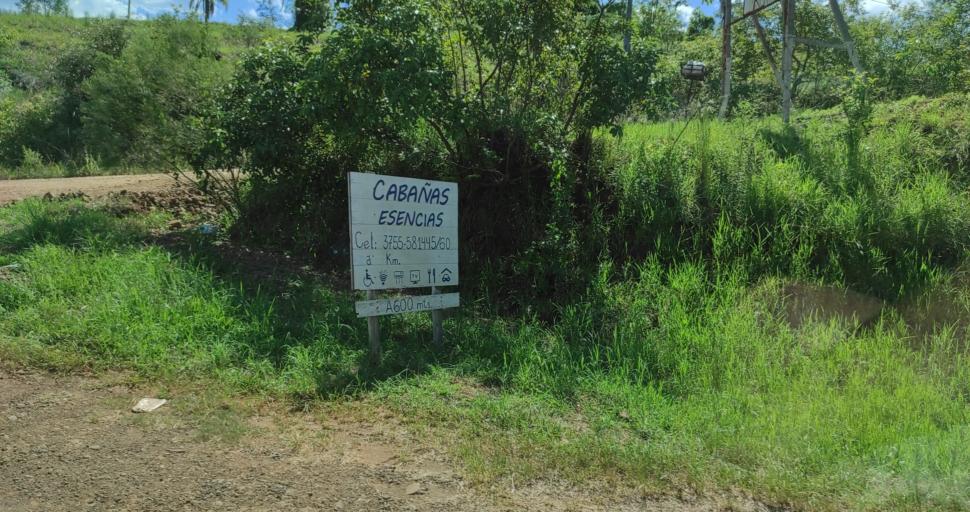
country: AR
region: Misiones
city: El Soberbio
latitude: -27.2783
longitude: -54.1967
